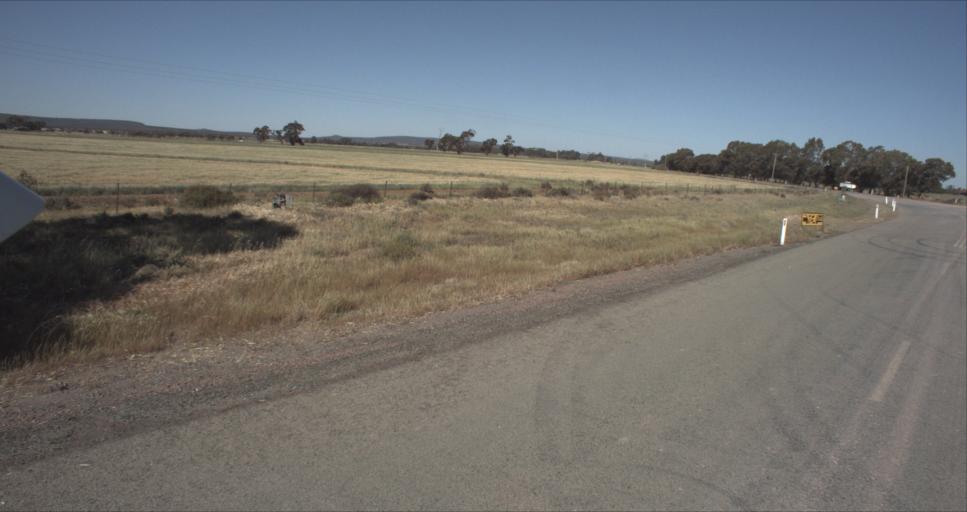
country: AU
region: New South Wales
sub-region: Leeton
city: Leeton
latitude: -34.4997
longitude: 146.3937
